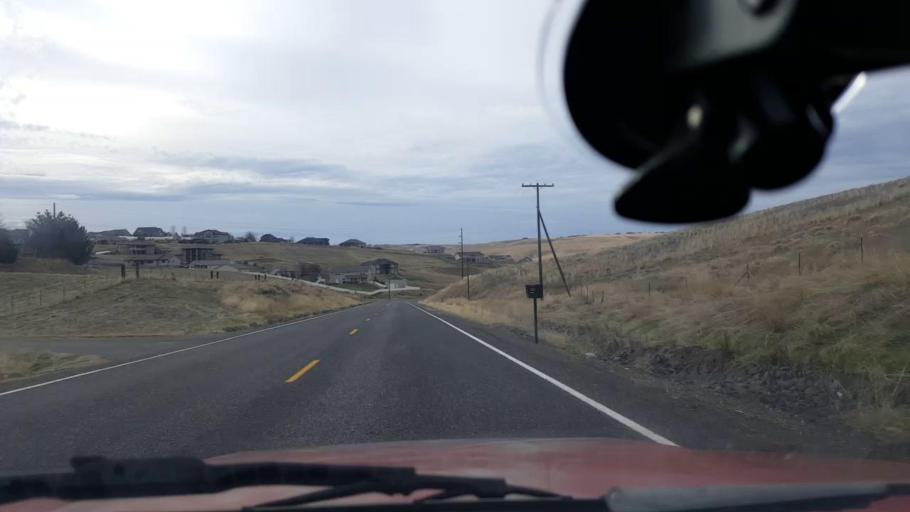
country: US
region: Washington
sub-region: Asotin County
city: Clarkston Heights-Vineland
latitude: 46.4011
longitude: -117.0899
